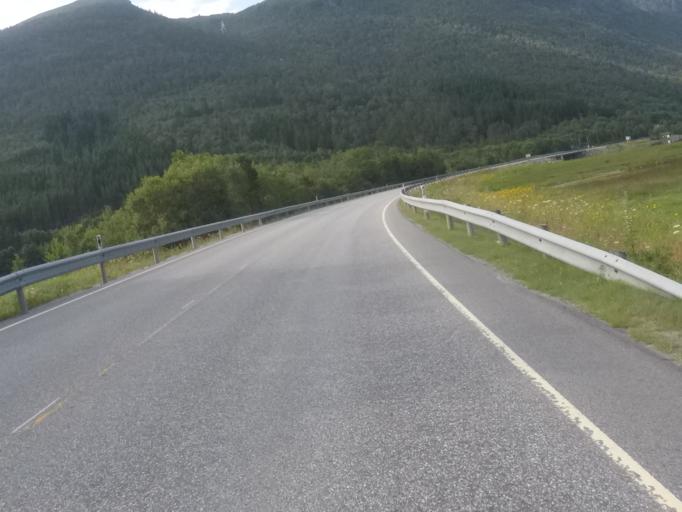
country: NO
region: More og Romsdal
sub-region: Rauma
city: Andalsnes
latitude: 62.5736
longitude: 7.7886
